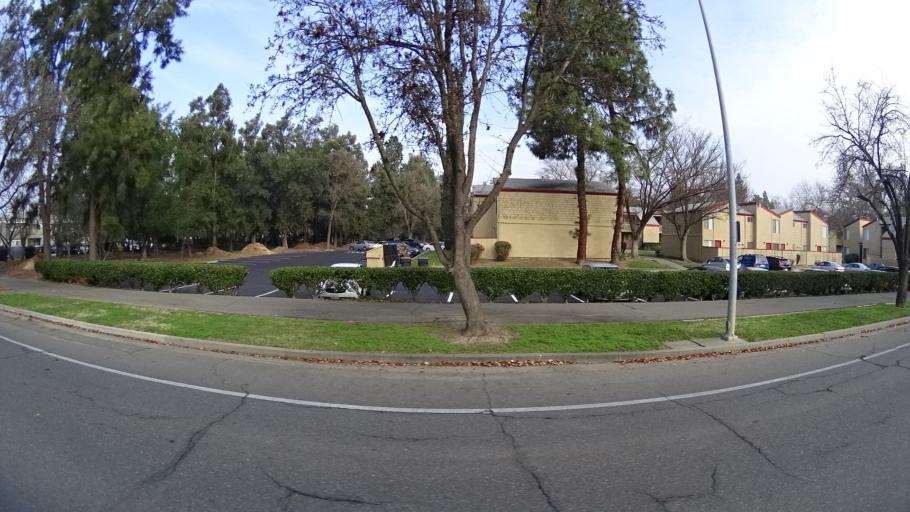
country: US
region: California
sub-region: Yolo County
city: Davis
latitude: 38.5609
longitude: -121.7548
